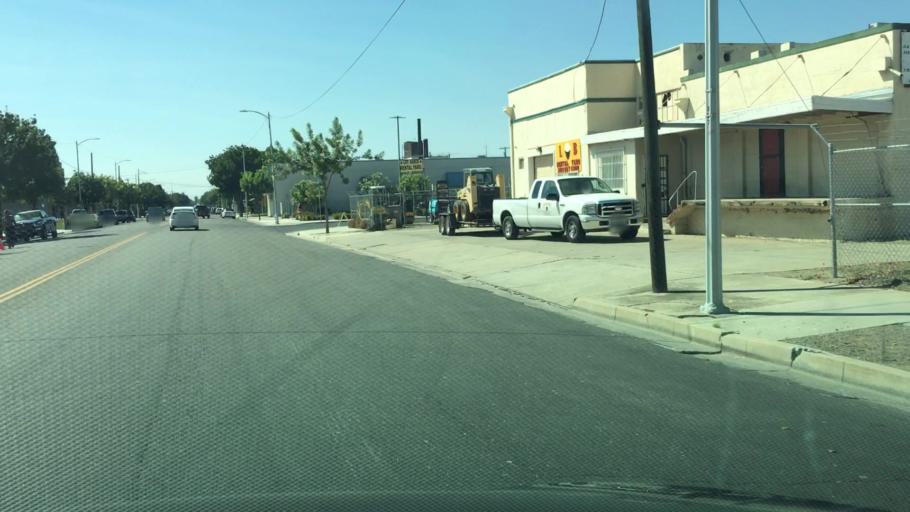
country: US
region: California
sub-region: Merced County
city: Los Banos
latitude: 37.0581
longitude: -120.8415
